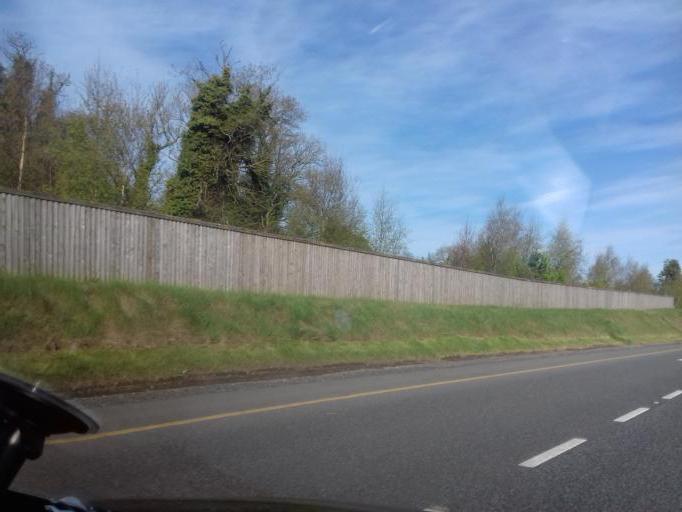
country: IE
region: Leinster
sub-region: An Mhi
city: Navan
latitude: 53.6436
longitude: -6.7454
